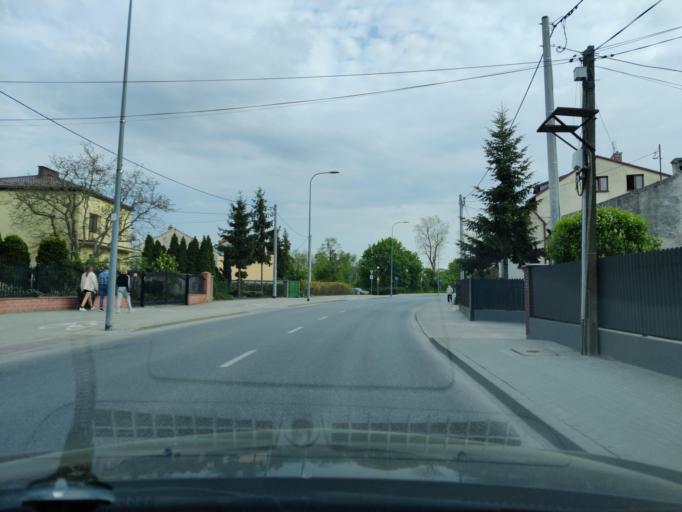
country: PL
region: Masovian Voivodeship
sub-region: Warszawa
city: Kabaty
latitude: 52.1295
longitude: 21.1037
